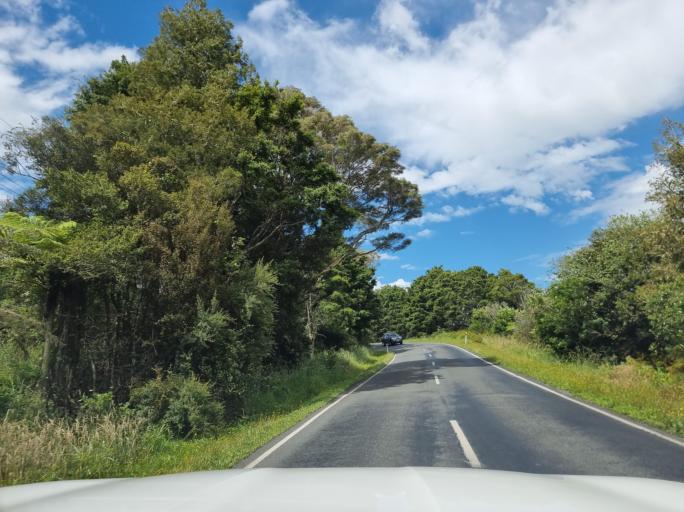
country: NZ
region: Northland
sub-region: Whangarei
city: Maungatapere
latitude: -35.9015
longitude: 174.2664
